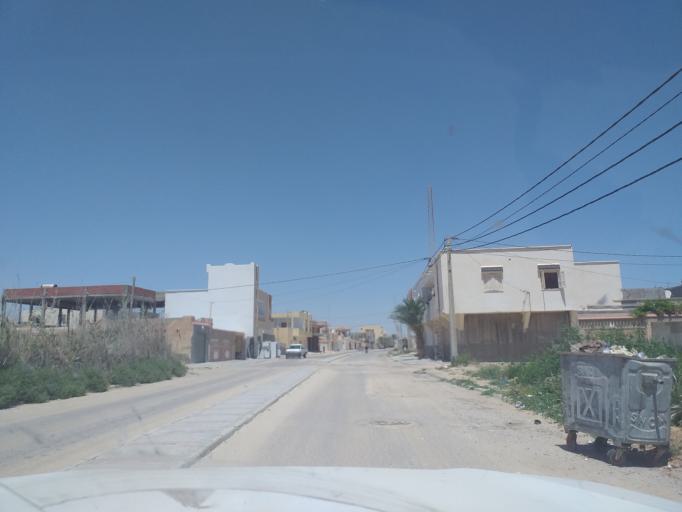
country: TN
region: Qabis
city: Gabes
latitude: 33.9438
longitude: 10.0740
